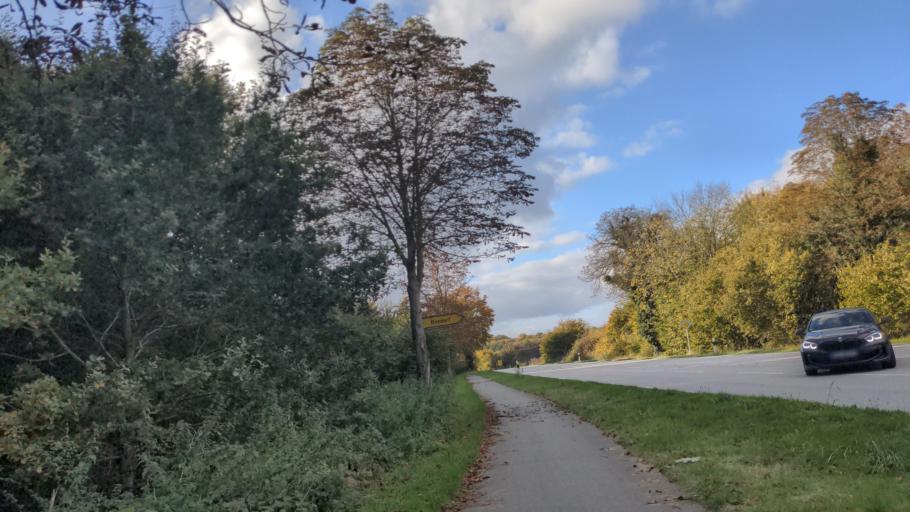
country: DE
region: Schleswig-Holstein
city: Bosdorf
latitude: 54.1393
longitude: 10.4883
